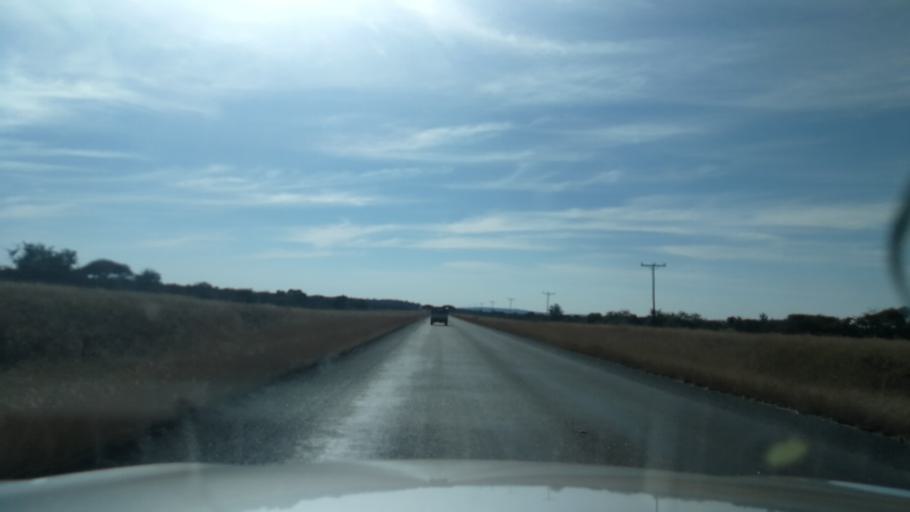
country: BW
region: South East
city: Janeng
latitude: -25.3478
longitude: 25.6266
